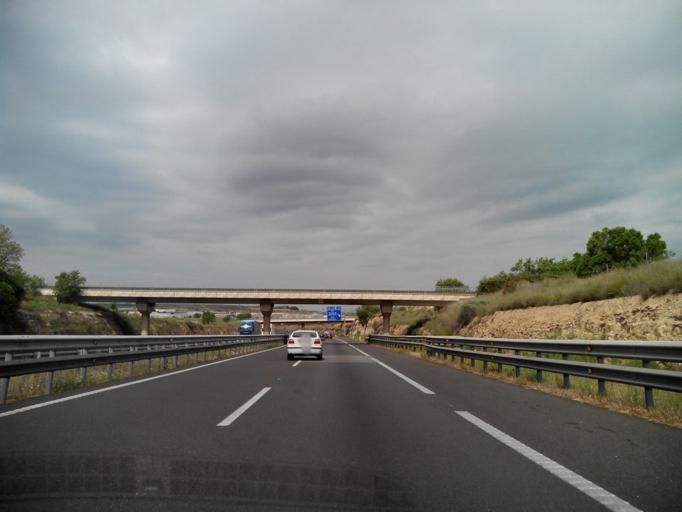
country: ES
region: Catalonia
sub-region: Provincia de Lleida
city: Tarrega
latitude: 41.6603
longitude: 1.1513
